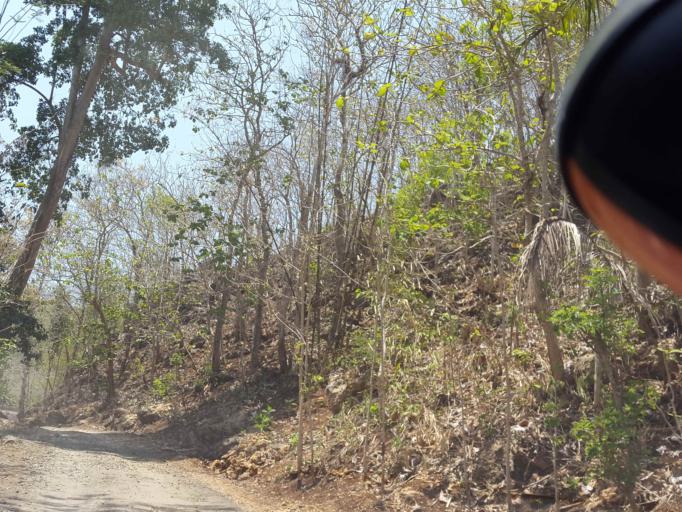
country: ID
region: East Java
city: Krajan
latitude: -8.2008
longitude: 110.9584
